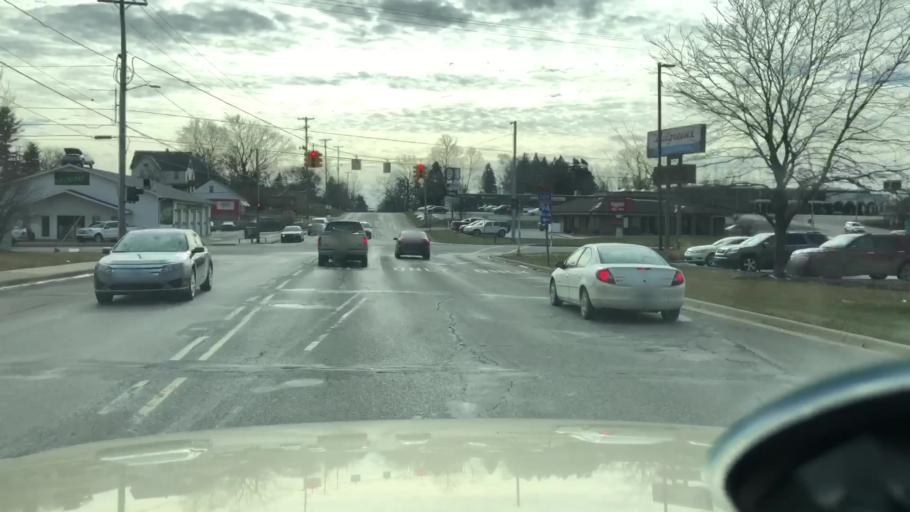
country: US
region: Michigan
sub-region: Jackson County
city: Jackson
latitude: 42.2563
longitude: -84.3650
